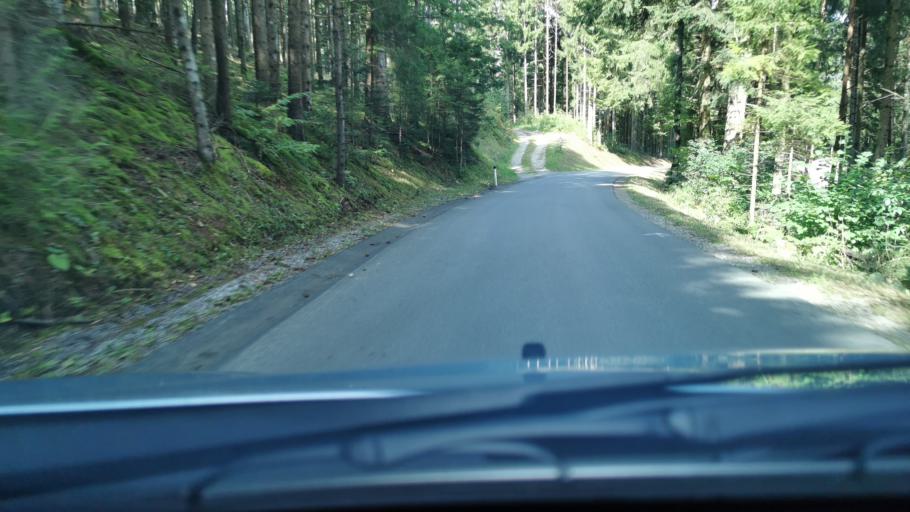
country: AT
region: Styria
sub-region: Politischer Bezirk Weiz
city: Birkfeld
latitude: 47.3365
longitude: 15.7051
